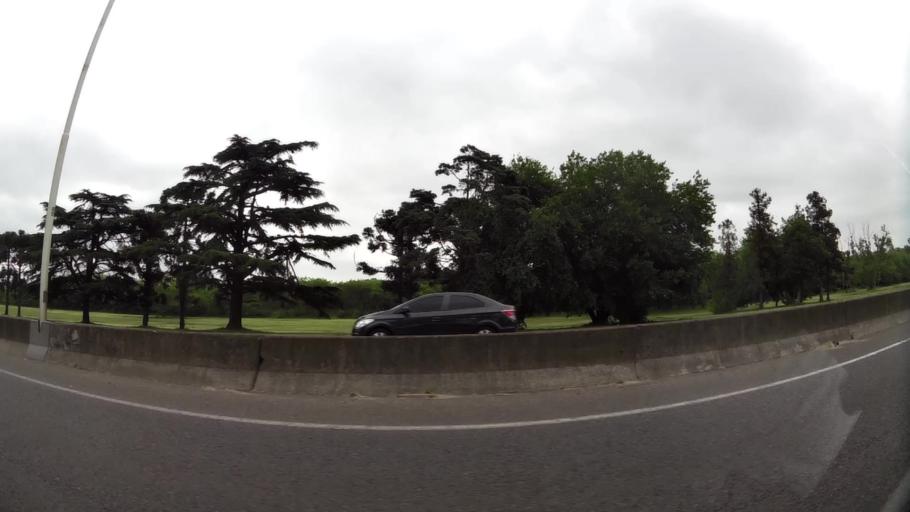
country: AR
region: Buenos Aires
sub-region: Partido de Ezeiza
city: Ezeiza
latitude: -34.7604
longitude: -58.5234
